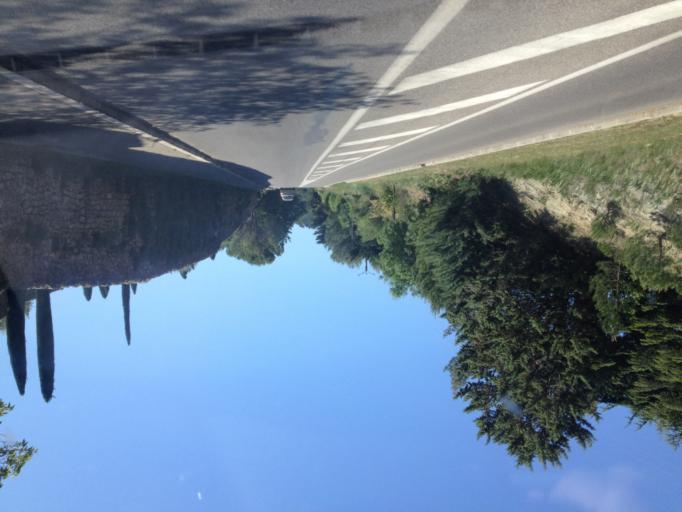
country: FR
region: Provence-Alpes-Cote d'Azur
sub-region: Departement du Vaucluse
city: Lourmarin
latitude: 43.7615
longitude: 5.3646
